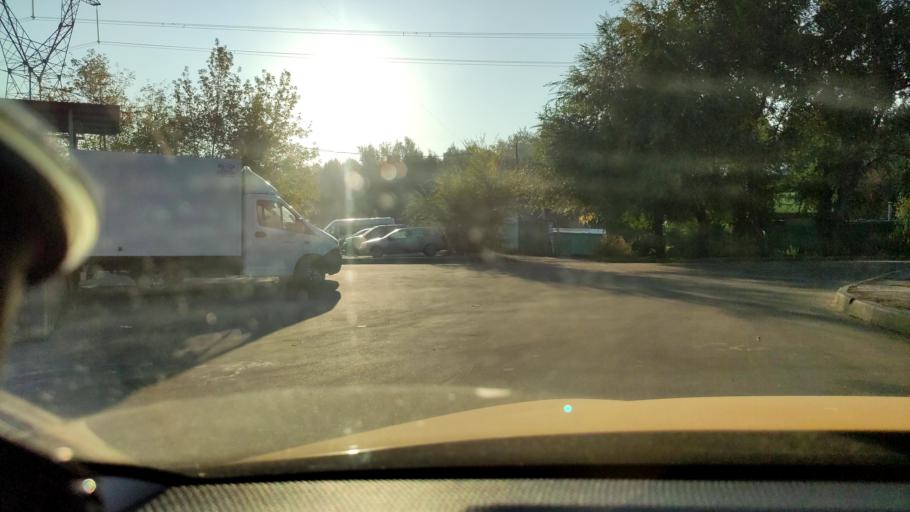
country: RU
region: Moscow
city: Vykhino-Zhulebino
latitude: 55.6931
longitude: 37.8230
